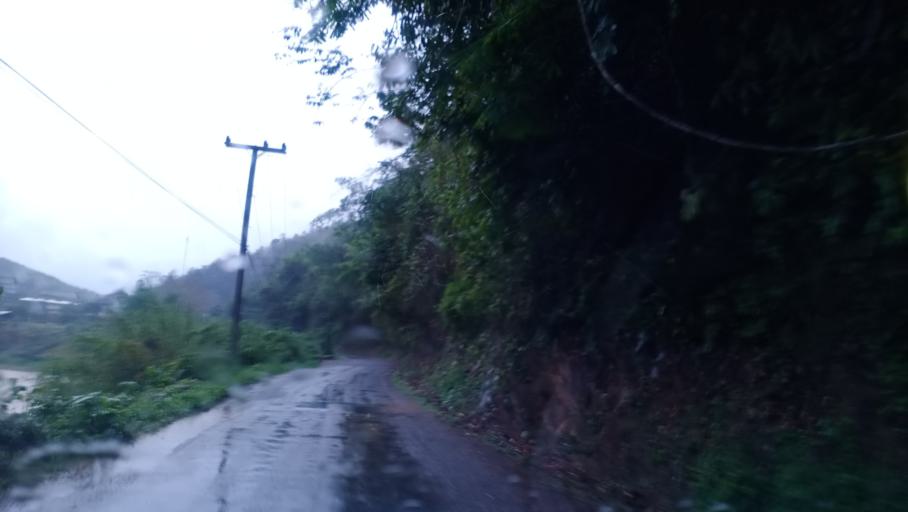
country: LA
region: Phongsali
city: Khoa
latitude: 21.0616
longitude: 102.4693
